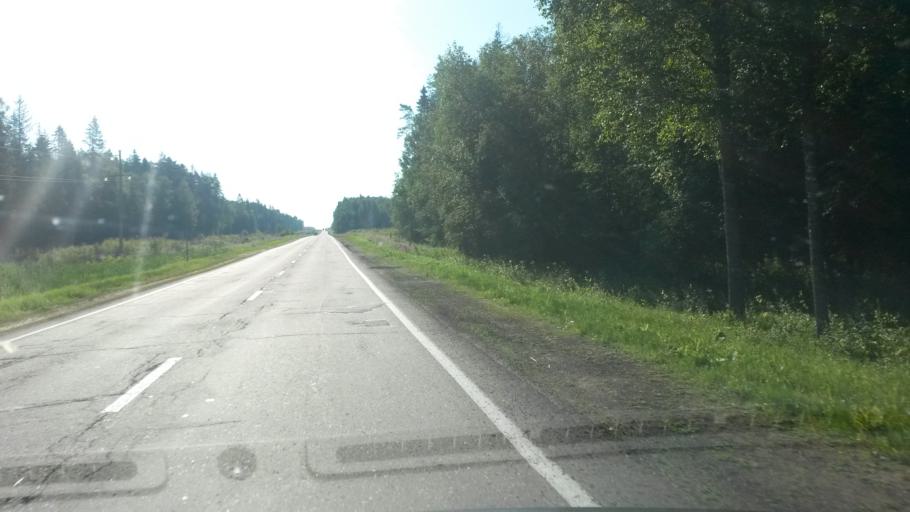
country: RU
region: Jaroslavl
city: Gavrilov-Yam
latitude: 57.2670
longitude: 39.9908
